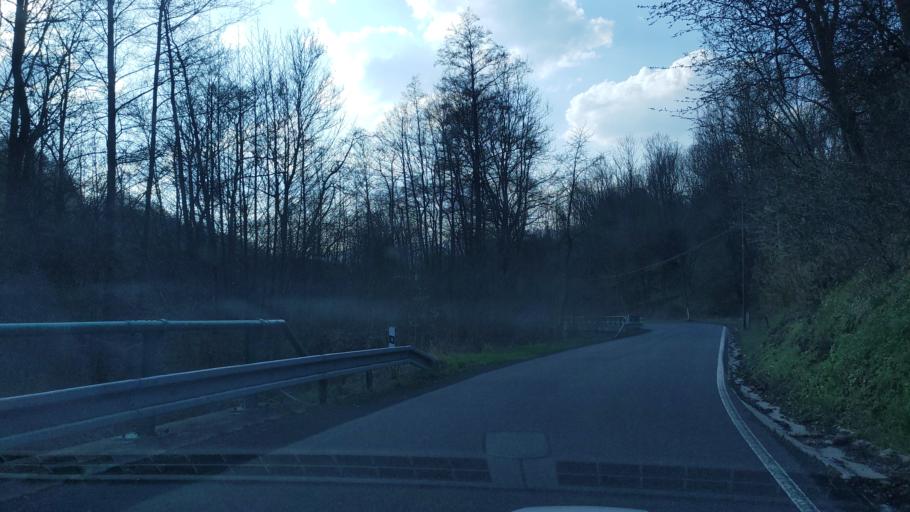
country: CZ
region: Ustecky
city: Povrly
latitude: 50.7049
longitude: 14.2267
